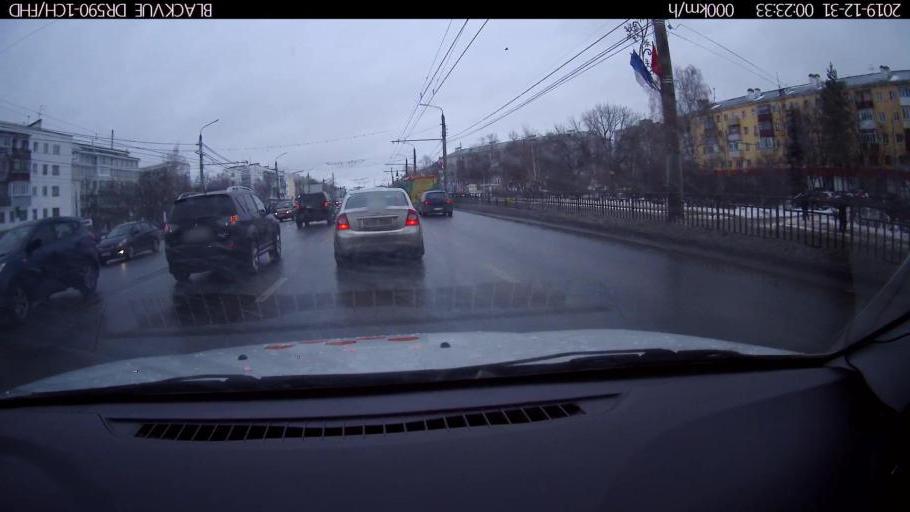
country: RU
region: Nizjnij Novgorod
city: Nizhniy Novgorod
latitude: 56.2886
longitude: 43.9307
